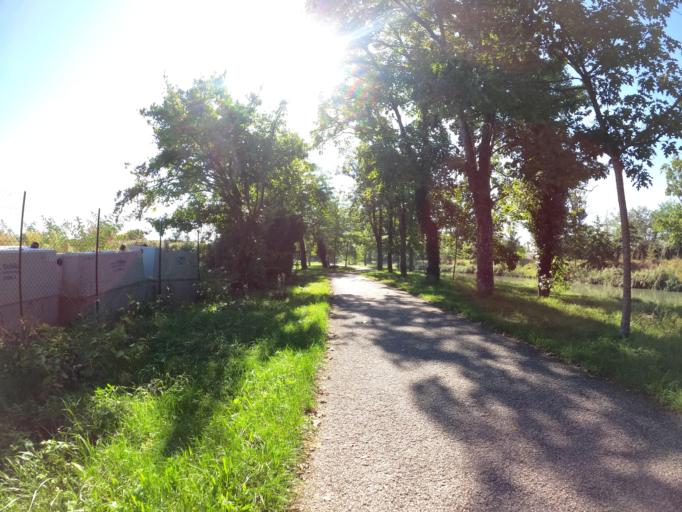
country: FR
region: Aquitaine
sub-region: Departement du Lot-et-Garonne
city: Bon-Encontre
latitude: 44.1870
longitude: 0.6527
